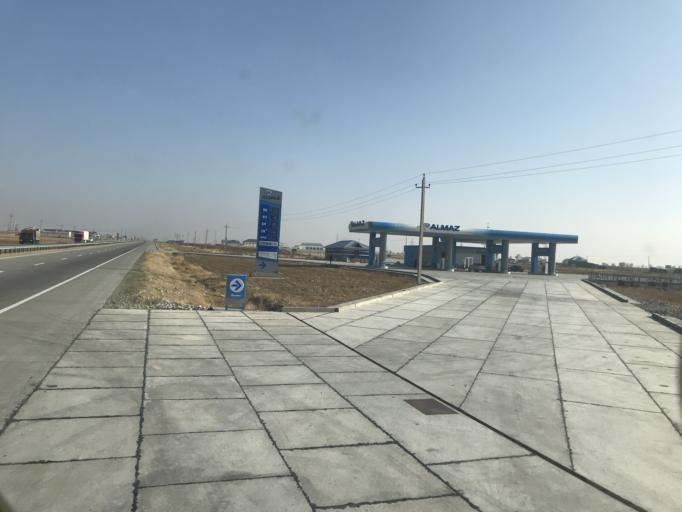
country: KZ
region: Ongtustik Qazaqstan
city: Shymkent
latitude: 42.4557
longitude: 69.6079
